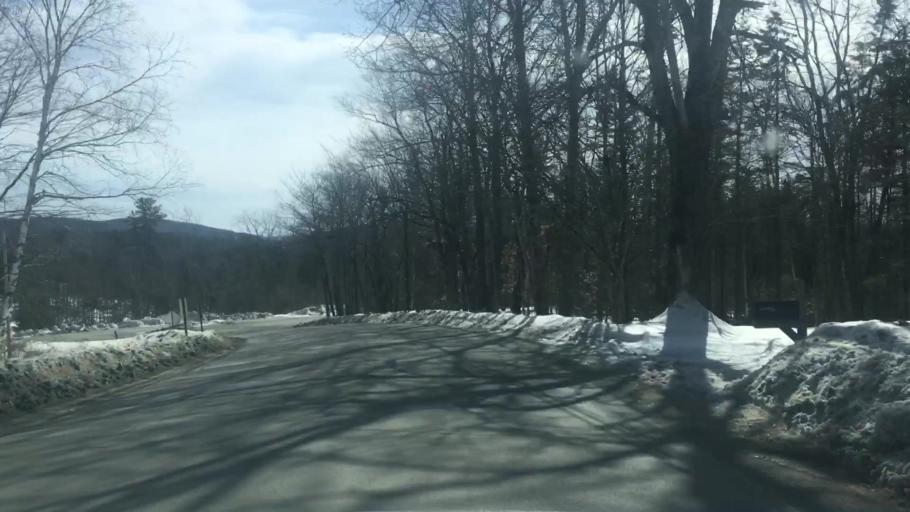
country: US
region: Maine
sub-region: Penobscot County
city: Holden
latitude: 44.7598
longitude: -68.6414
